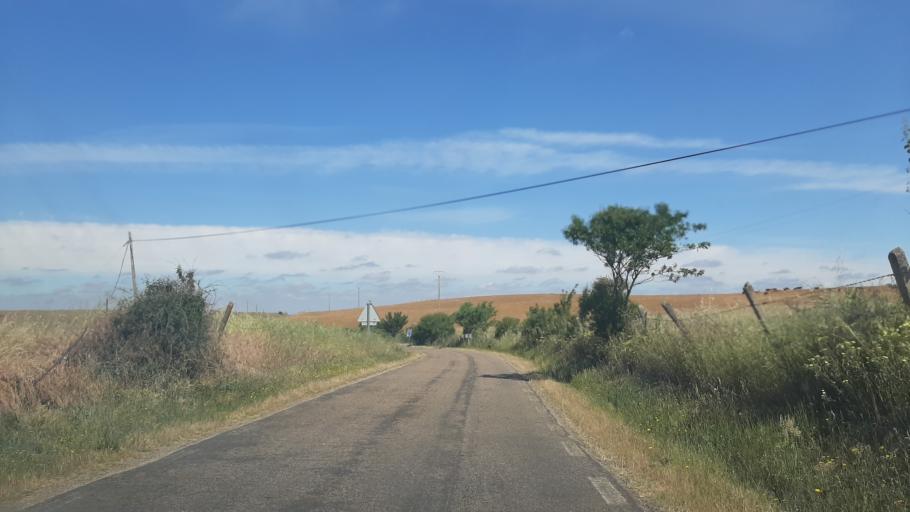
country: ES
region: Castille and Leon
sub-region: Provincia de Salamanca
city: Zamarra
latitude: 40.5225
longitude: -6.4558
